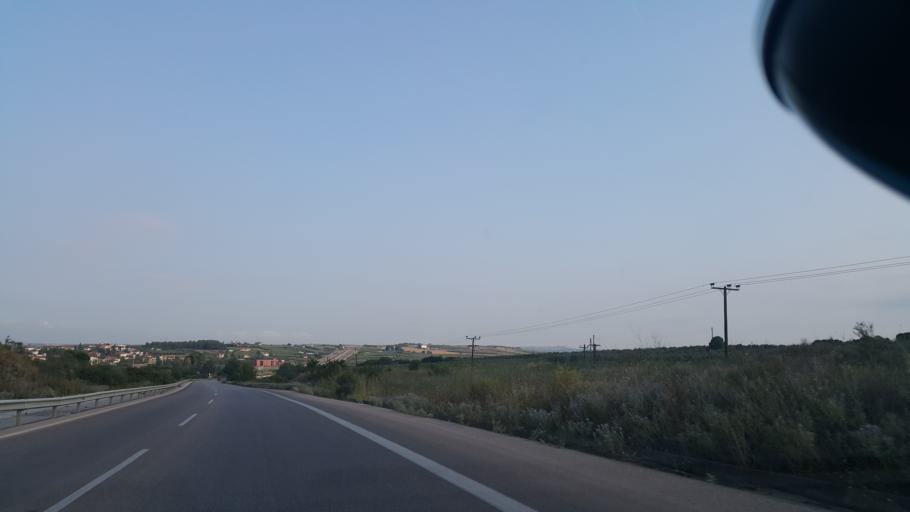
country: GR
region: Central Macedonia
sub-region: Nomos Chalkidikis
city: Nea Kallikrateia
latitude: 40.3341
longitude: 23.0751
